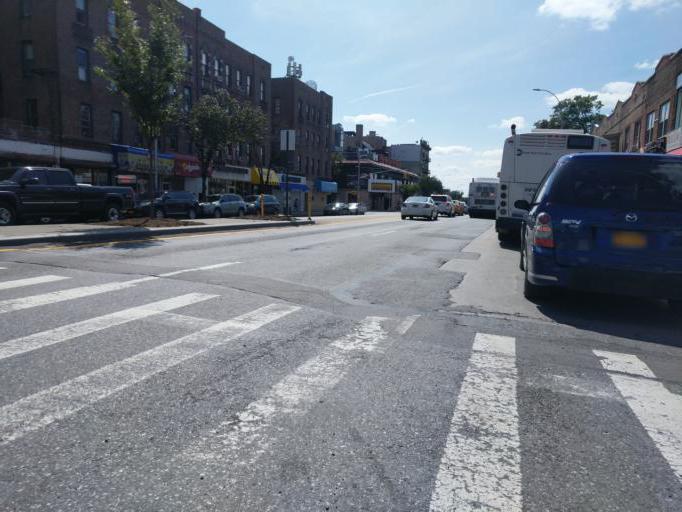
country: US
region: New York
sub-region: Queens County
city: Long Island City
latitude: 40.7558
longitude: -73.8836
